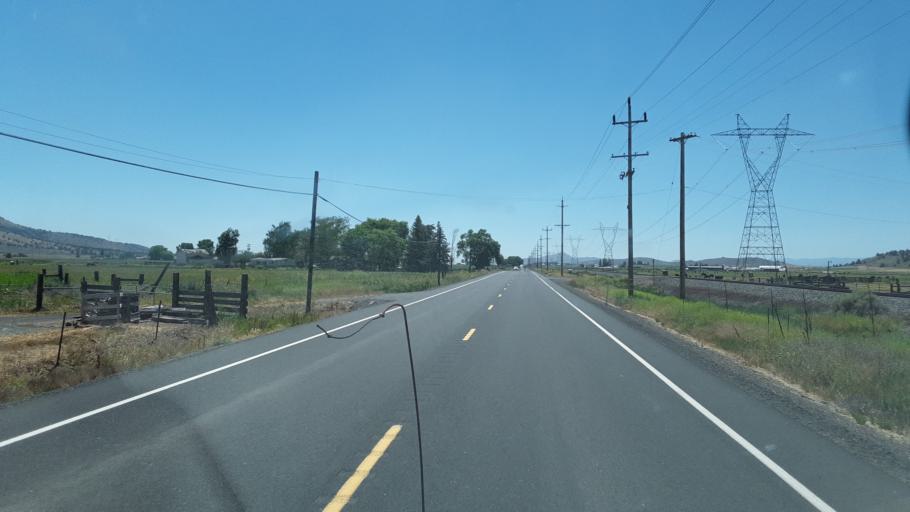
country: US
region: Oregon
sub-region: Klamath County
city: Altamont
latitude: 42.0938
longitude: -121.6892
